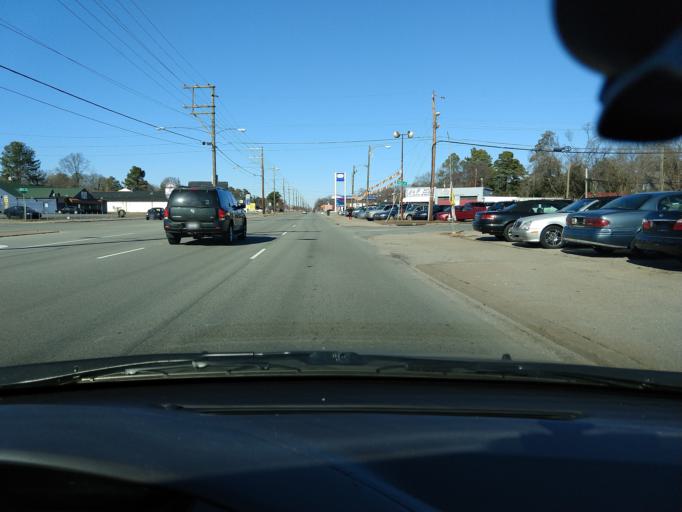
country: US
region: Virginia
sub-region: Chesterfield County
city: Bensley
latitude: 37.4651
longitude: -77.4428
